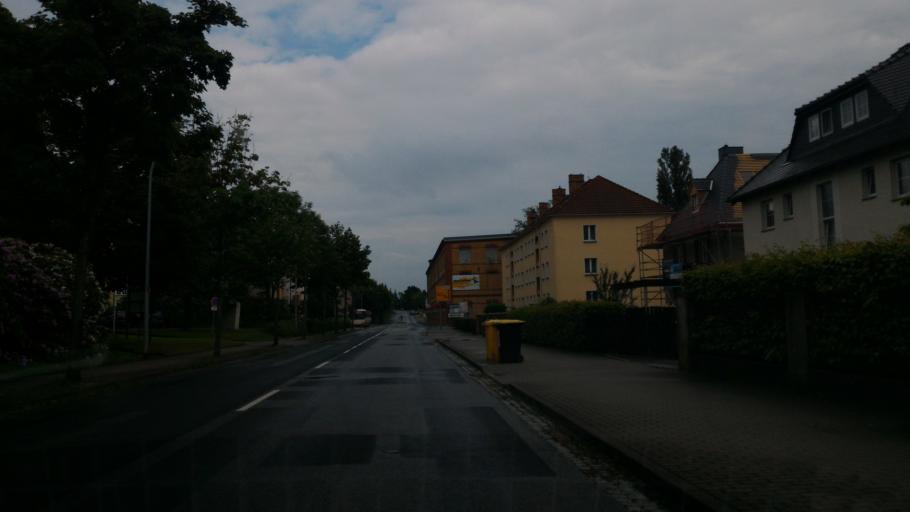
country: DE
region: Saxony
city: Olbersdorf
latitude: 50.8995
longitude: 14.7785
